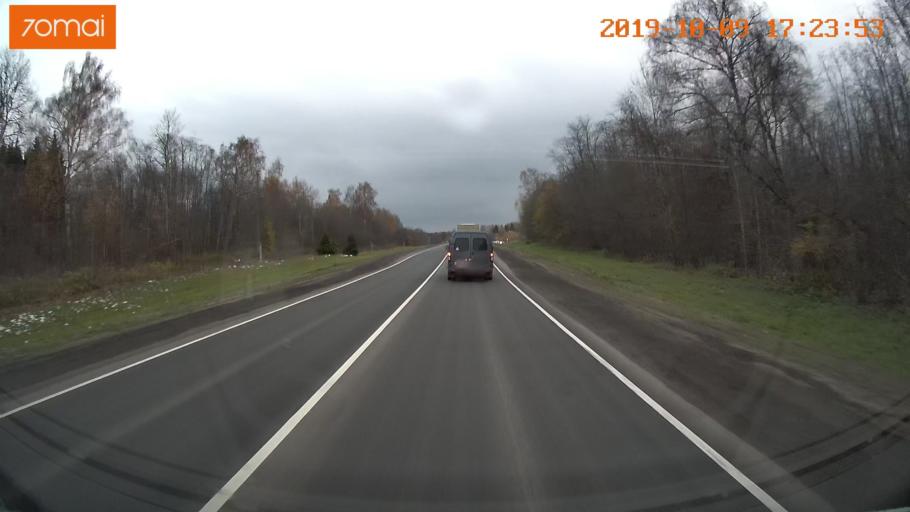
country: RU
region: Ivanovo
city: Furmanov
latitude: 57.1903
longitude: 41.1129
